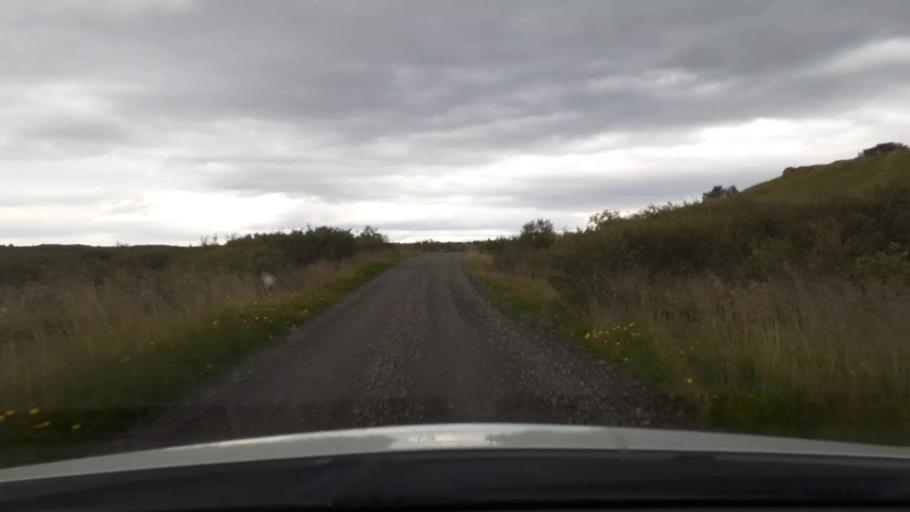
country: IS
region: West
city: Borgarnes
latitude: 64.6397
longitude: -21.7516
